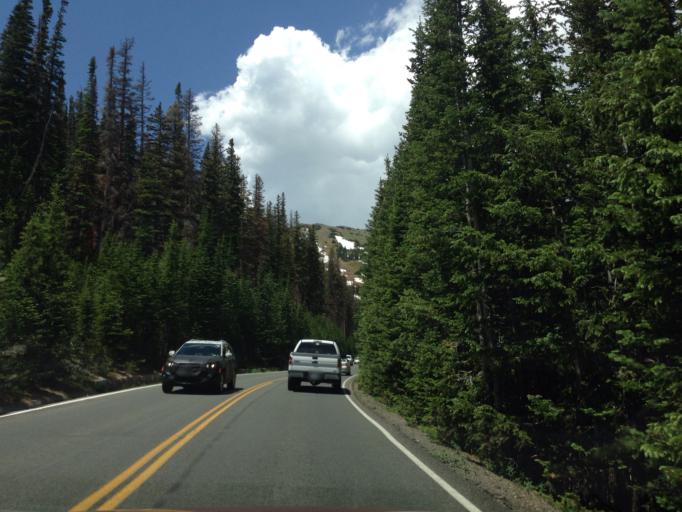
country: US
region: Colorado
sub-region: Larimer County
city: Estes Park
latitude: 40.3874
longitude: -105.6695
